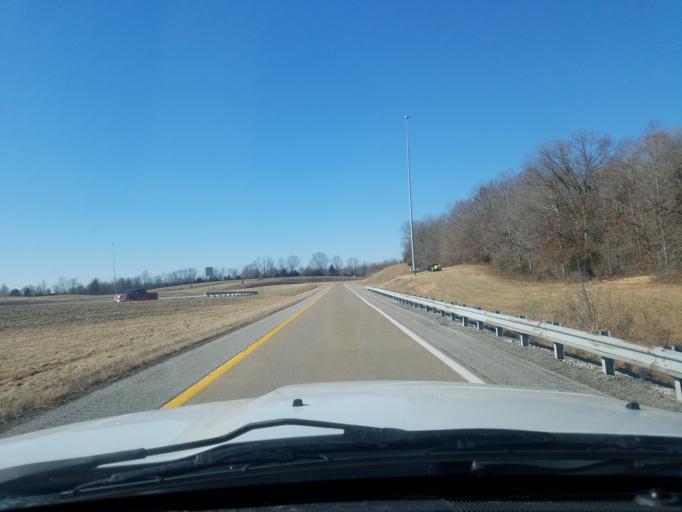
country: US
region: Kentucky
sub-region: Ohio County
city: Oak Grove
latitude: 37.3867
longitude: -86.8072
